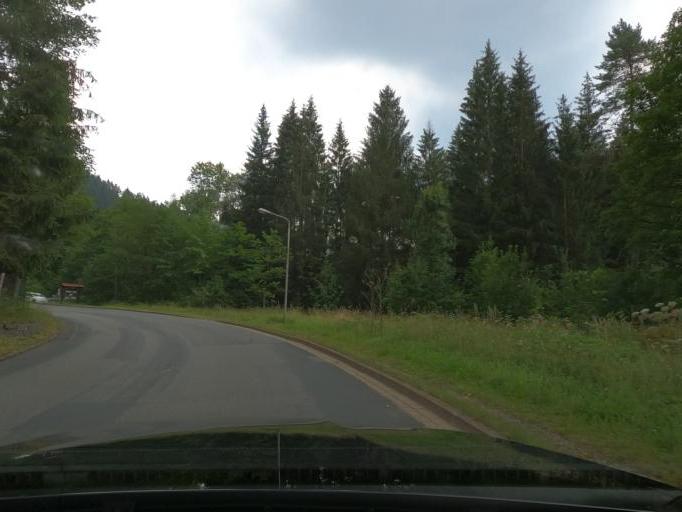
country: DE
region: Lower Saxony
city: Wildemann
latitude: 51.8201
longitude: 10.2726
